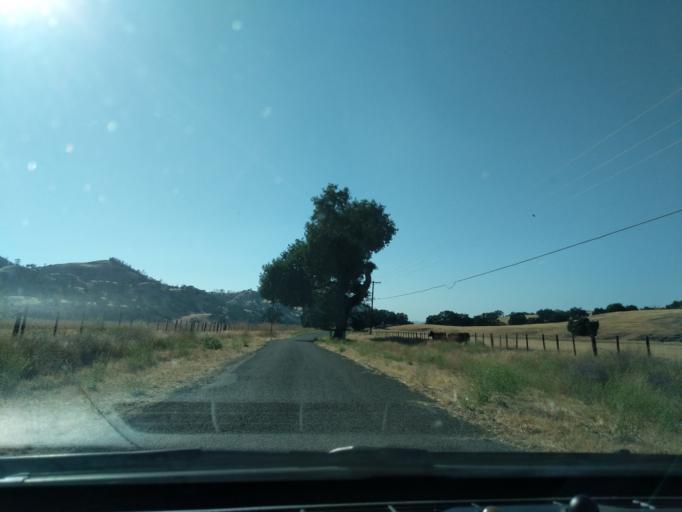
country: US
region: California
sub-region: San Luis Obispo County
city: San Miguel
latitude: 36.1152
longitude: -120.7257
